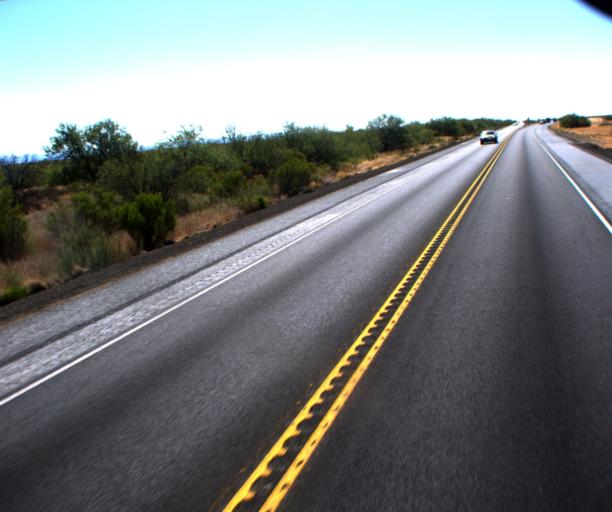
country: US
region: Arizona
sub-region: Yavapai County
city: Congress
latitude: 34.1035
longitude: -112.9219
